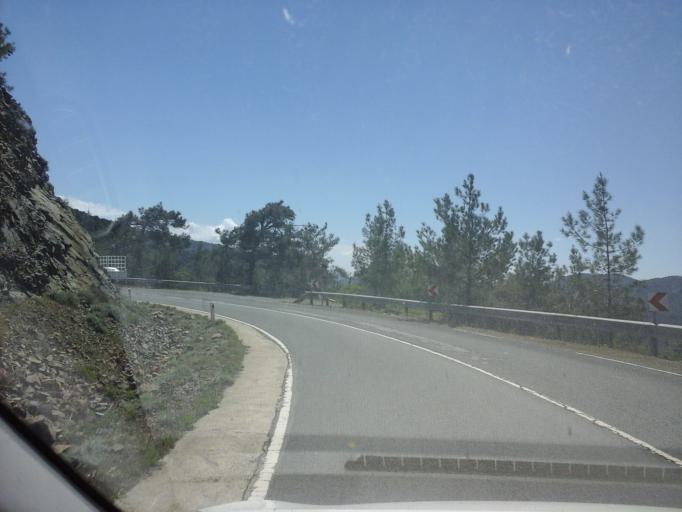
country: CY
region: Lefkosia
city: Kakopetria
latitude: 35.0011
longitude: 32.7898
